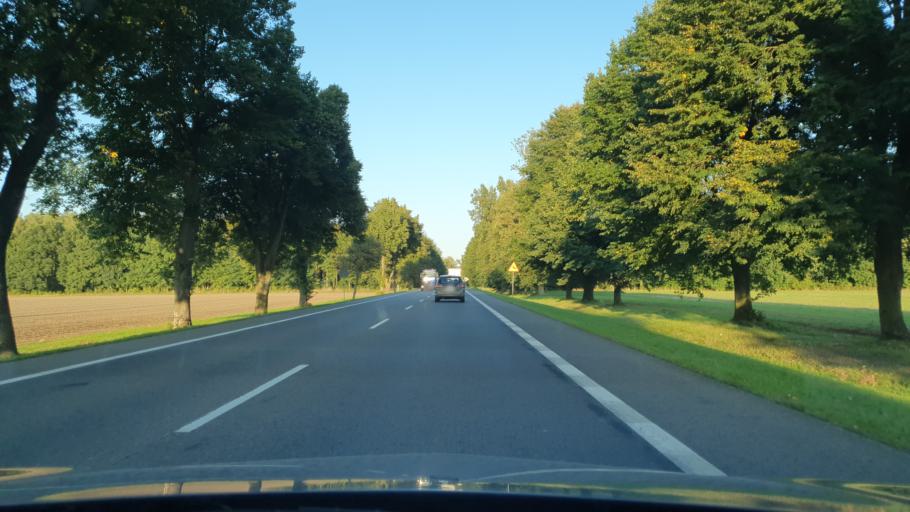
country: PL
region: Pomeranian Voivodeship
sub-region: Powiat slupski
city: Kobylnica
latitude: 54.4320
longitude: 16.8919
